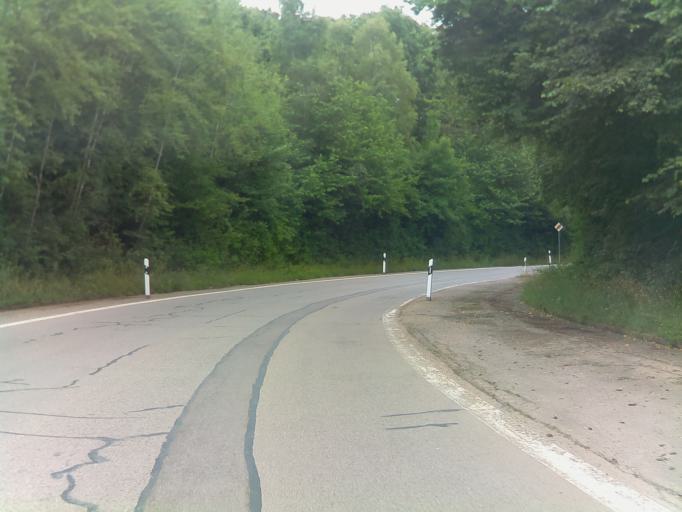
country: DE
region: Saarland
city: Merchweiler
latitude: 49.3440
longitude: 7.0448
